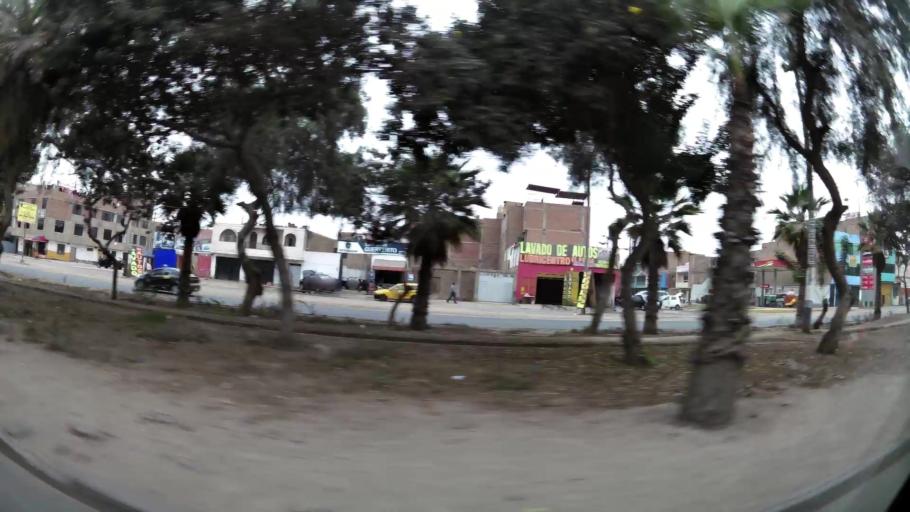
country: PE
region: Lima
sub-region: Lima
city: Urb. Santo Domingo
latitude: -11.9206
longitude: -77.0508
